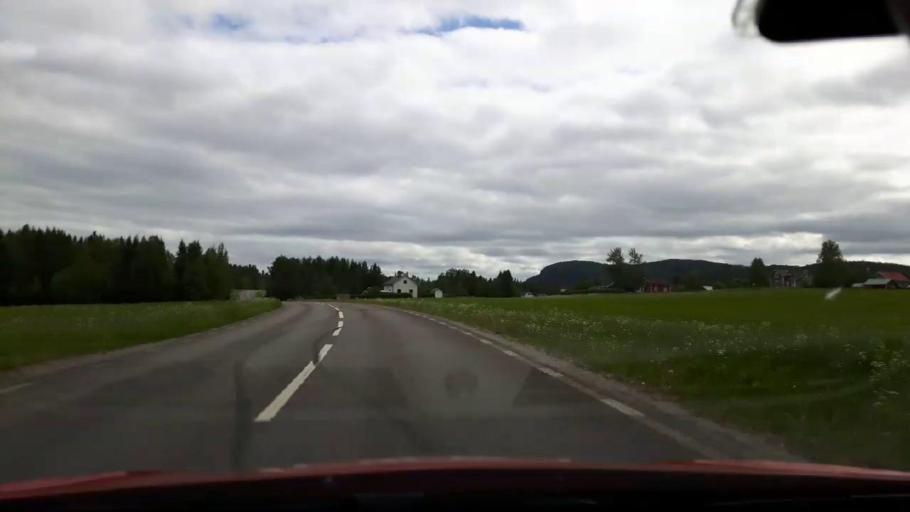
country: SE
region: Jaemtland
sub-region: Ragunda Kommun
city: Hammarstrand
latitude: 63.0912
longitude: 16.3588
